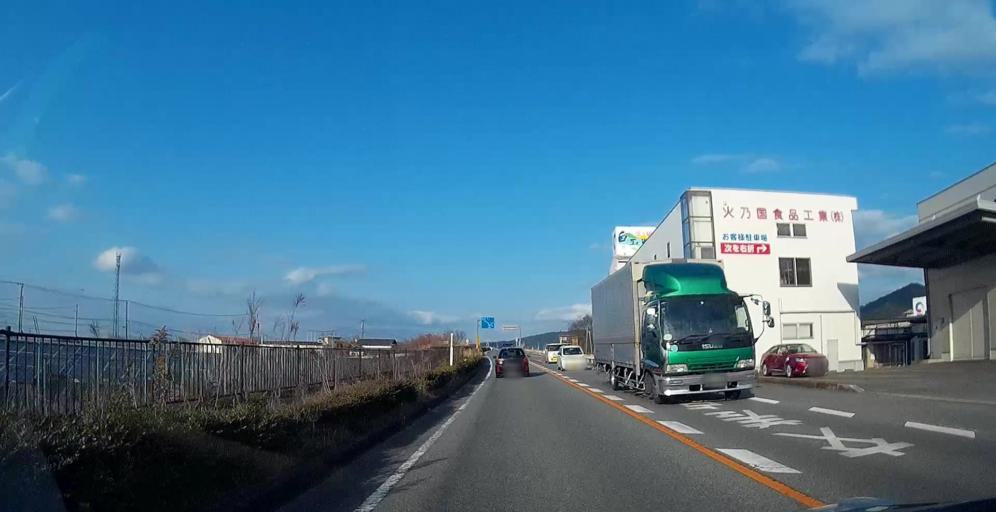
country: JP
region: Kumamoto
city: Matsubase
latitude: 32.5852
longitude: 130.7008
